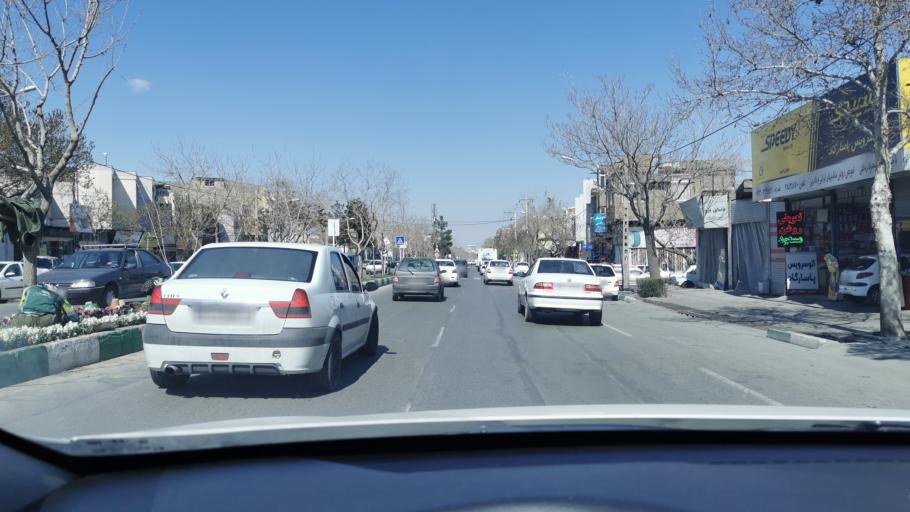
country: IR
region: Razavi Khorasan
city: Mashhad
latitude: 36.2719
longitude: 59.5757
